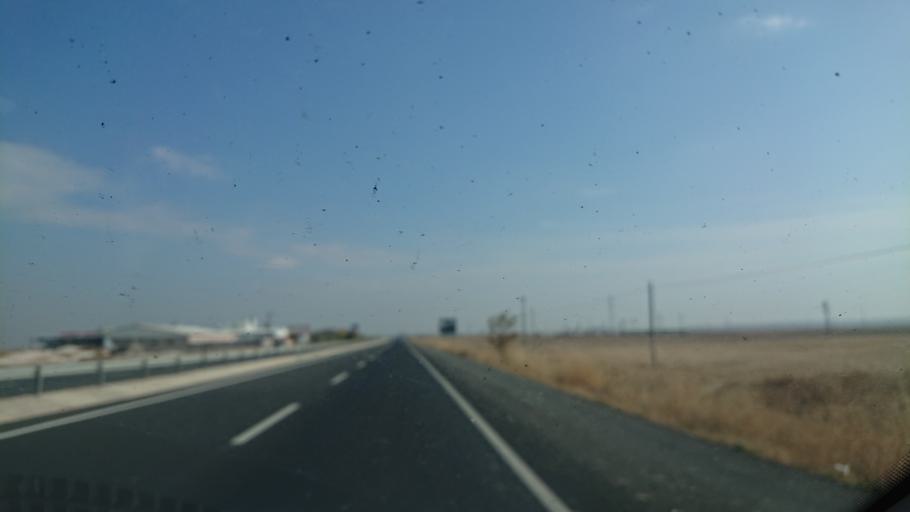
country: TR
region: Aksaray
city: Yesilova
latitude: 38.3125
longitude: 33.8408
